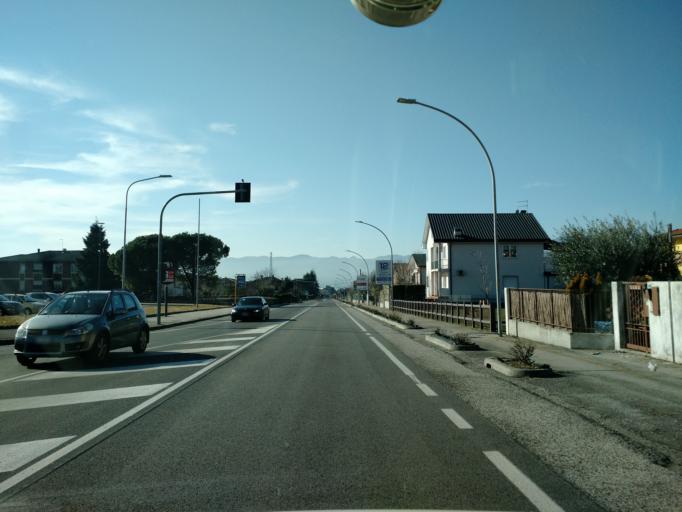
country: IT
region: Veneto
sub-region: Provincia di Vicenza
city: Piovene Rocchette
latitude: 45.7478
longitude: 11.4250
